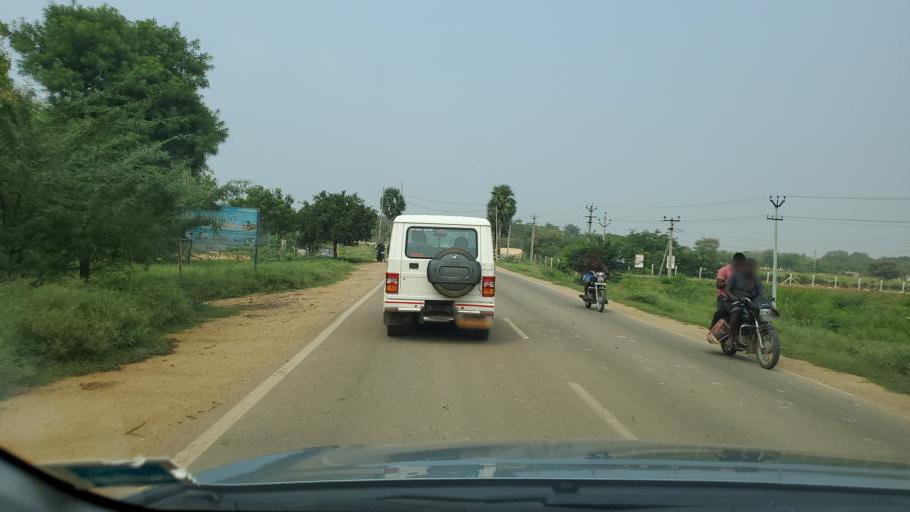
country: IN
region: Tamil Nadu
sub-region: Ariyalur
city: Ariyalur
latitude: 11.1232
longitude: 79.1428
